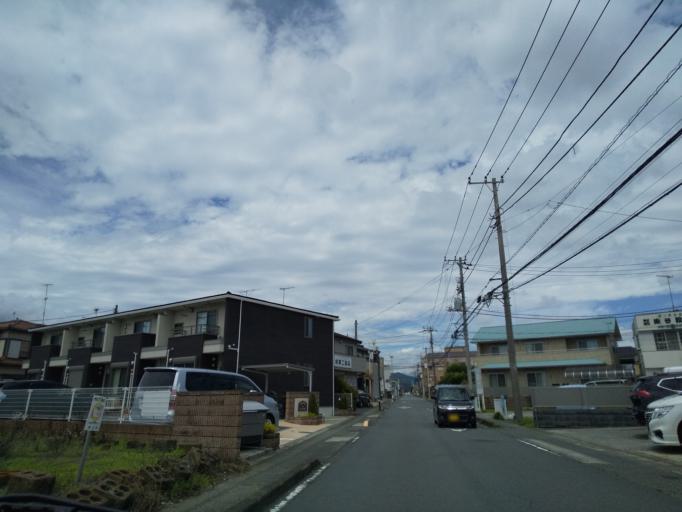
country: JP
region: Kanagawa
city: Zama
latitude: 35.5167
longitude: 139.3351
